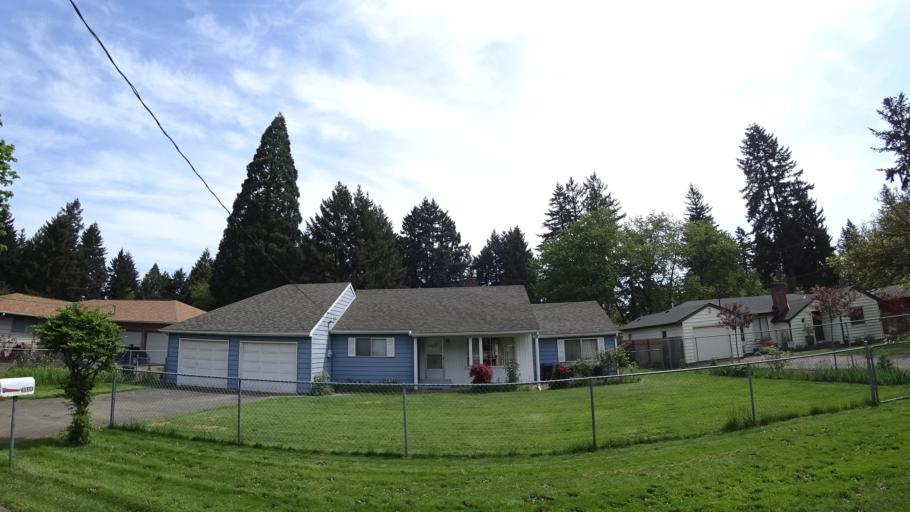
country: US
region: Oregon
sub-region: Clackamas County
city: Oatfield
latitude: 45.4505
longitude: -122.6026
